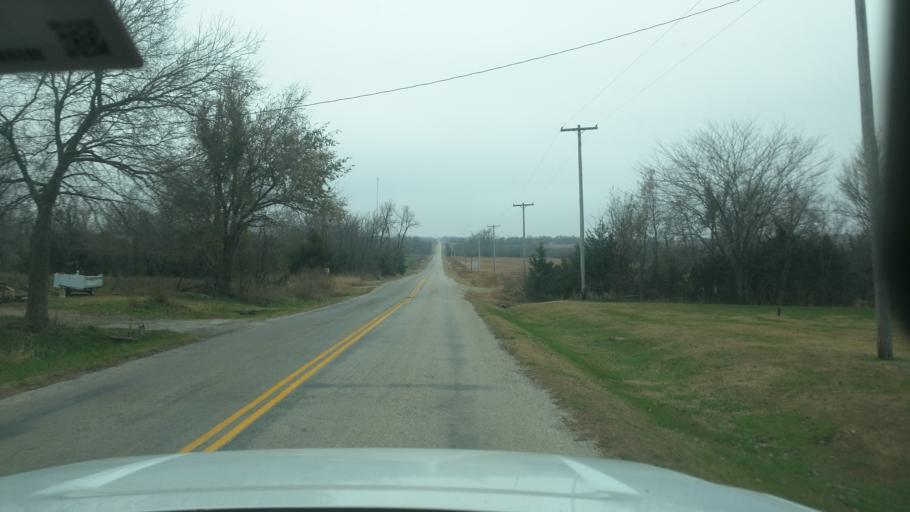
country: US
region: Kansas
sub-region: Morris County
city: Council Grove
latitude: 38.6429
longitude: -96.2615
